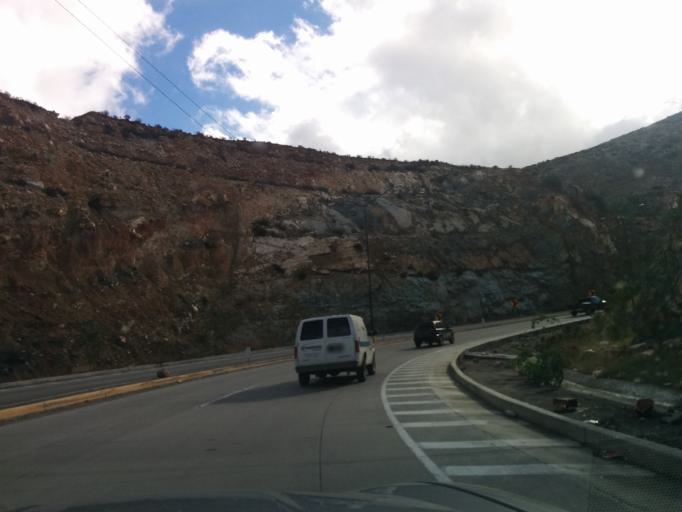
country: MX
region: Baja California
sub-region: Tijuana
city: Ejido Javier Rojo Gomez
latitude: 32.5423
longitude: -116.8531
